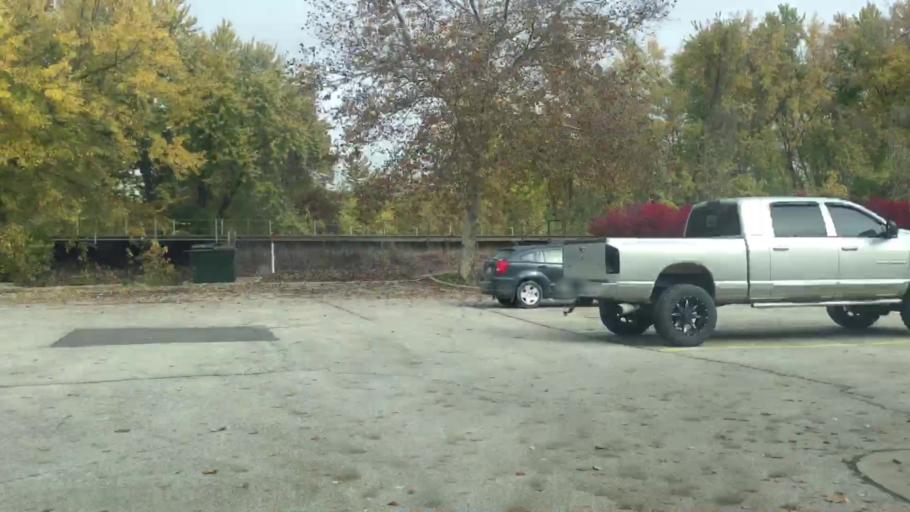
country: US
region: Missouri
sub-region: Gasconade County
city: Hermann
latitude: 38.7067
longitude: -91.4305
